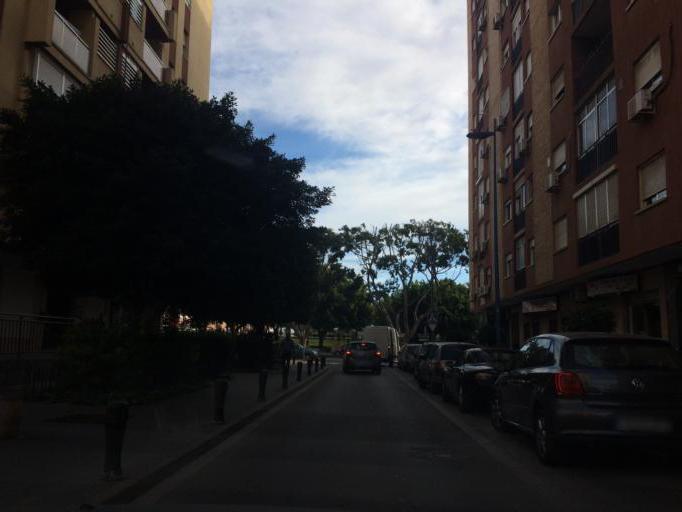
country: ES
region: Andalusia
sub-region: Provincia de Almeria
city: Almeria
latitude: 36.8418
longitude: -2.4481
